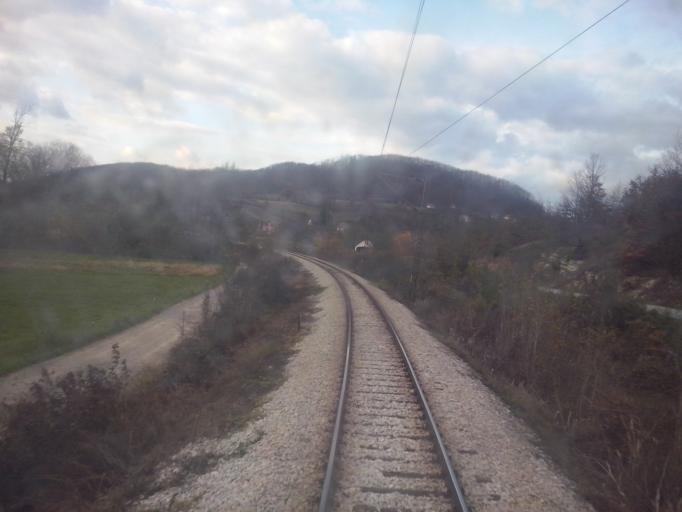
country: RS
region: Central Serbia
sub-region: Zlatiborski Okrug
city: Kosjeric
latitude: 43.9750
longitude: 19.9534
